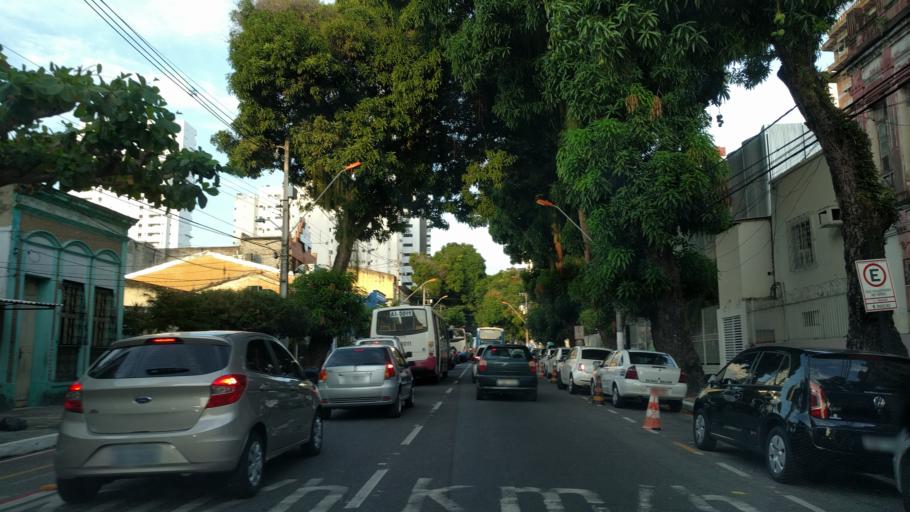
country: BR
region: Para
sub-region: Belem
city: Belem
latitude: -1.4634
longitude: -48.4912
